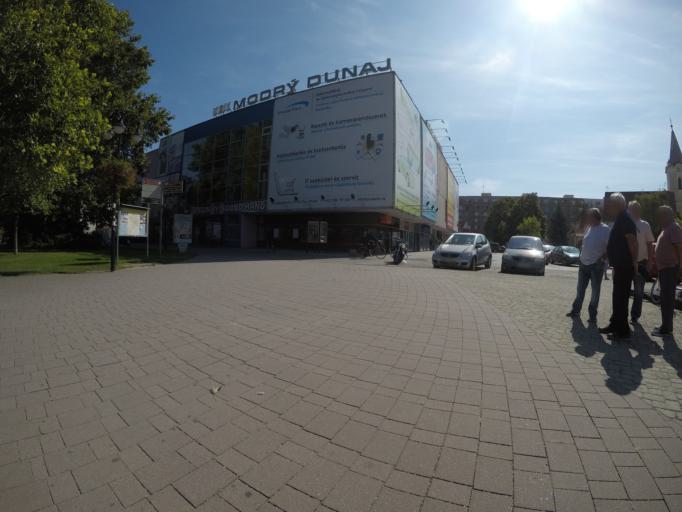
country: SK
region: Trnavsky
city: Dunajska Streda
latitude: 47.9933
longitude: 17.6166
